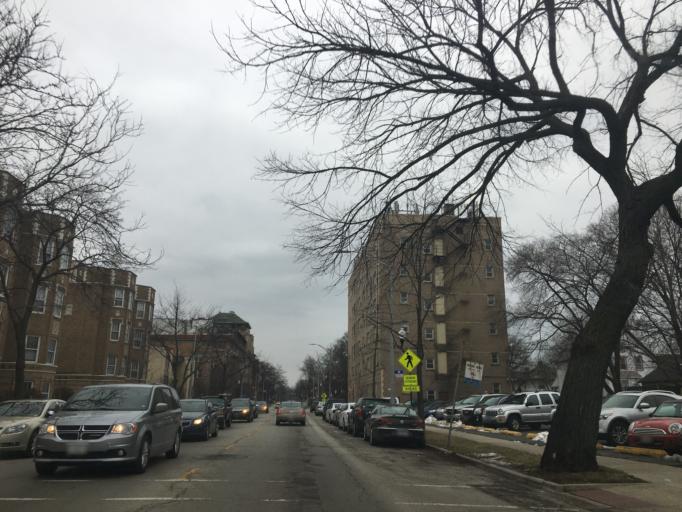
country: US
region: Illinois
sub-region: Cook County
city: Oak Park
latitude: 41.8890
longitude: -87.7750
